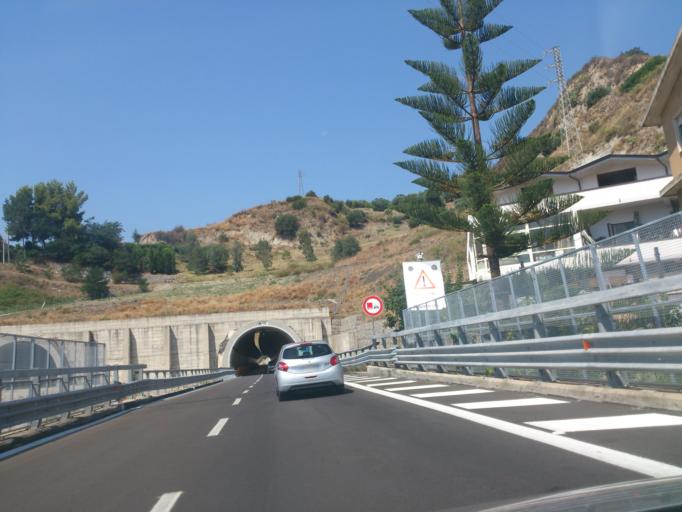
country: IT
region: Calabria
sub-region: Provincia di Reggio Calabria
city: Roccella Ionica
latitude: 38.3301
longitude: 16.4072
